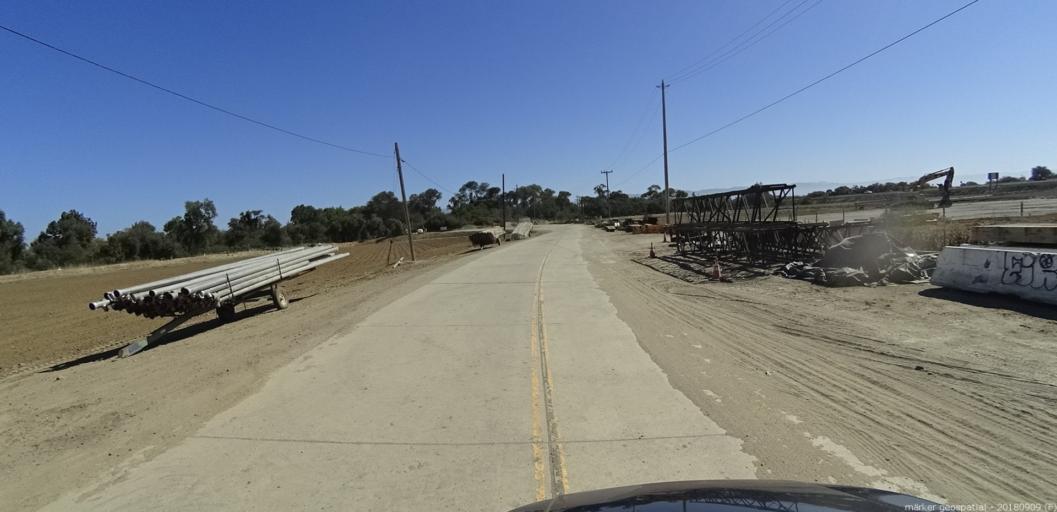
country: US
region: California
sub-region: Monterey County
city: Salinas
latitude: 36.6277
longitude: -121.6812
